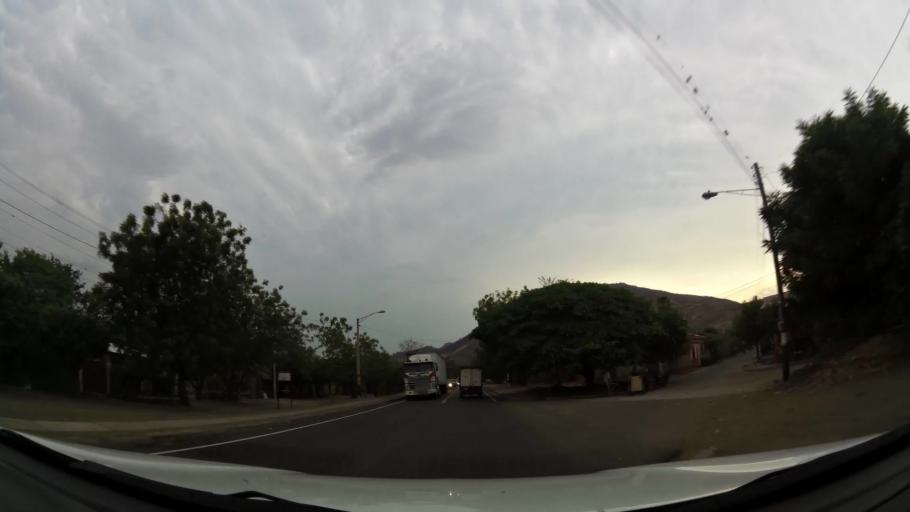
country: NI
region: Matagalpa
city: Ciudad Dario
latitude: 12.9281
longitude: -86.1963
